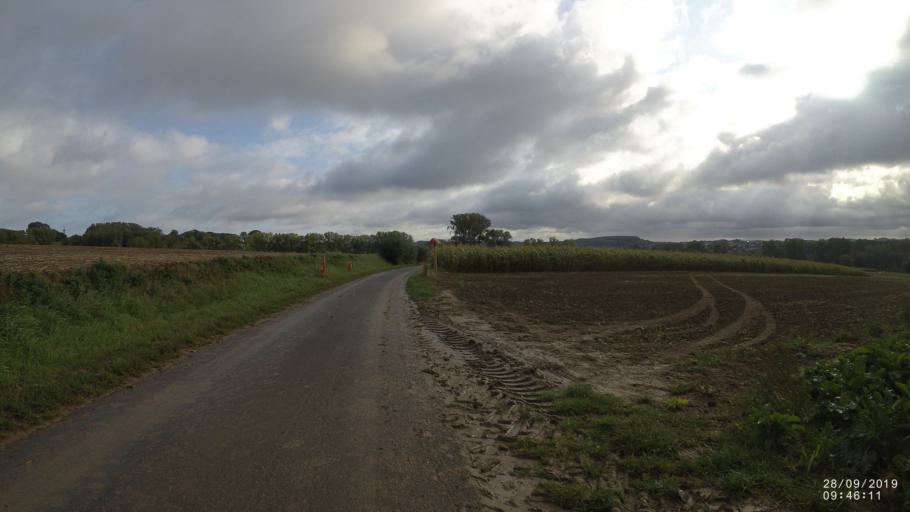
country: BE
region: Wallonia
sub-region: Province du Hainaut
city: Flobecq
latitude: 50.8004
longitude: 3.7343
